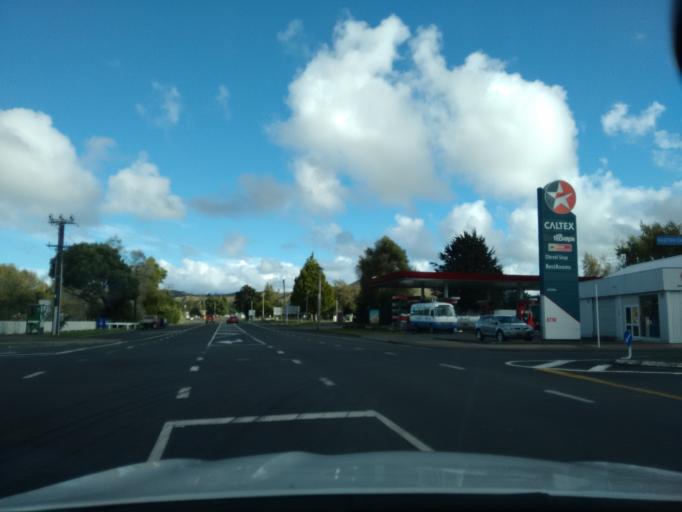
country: NZ
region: Manawatu-Wanganui
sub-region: Ruapehu District
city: Waiouru
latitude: -39.4275
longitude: 175.2818
